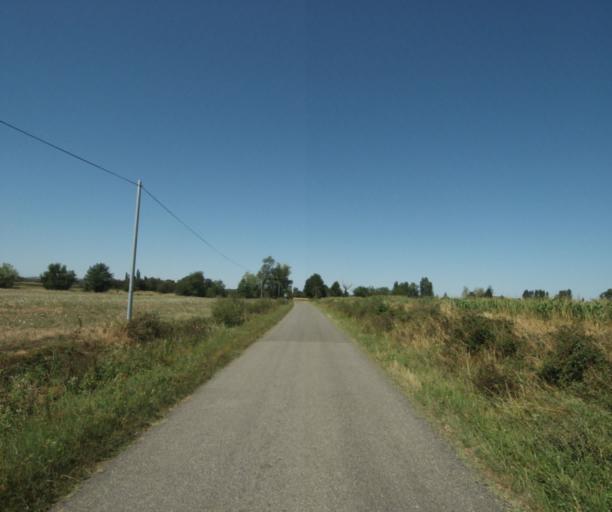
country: FR
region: Midi-Pyrenees
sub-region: Departement de la Haute-Garonne
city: Revel
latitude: 43.4741
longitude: 1.9837
